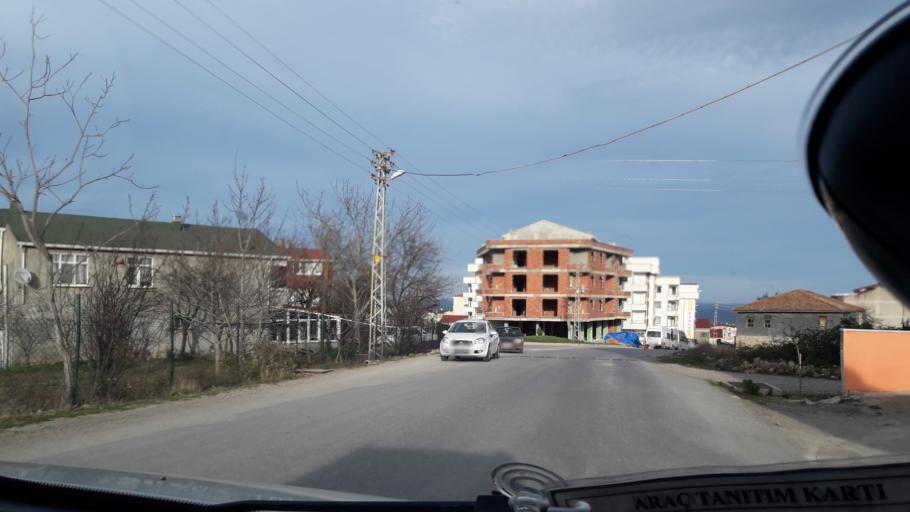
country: TR
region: Sinop
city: Gerze
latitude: 41.8033
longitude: 35.1822
